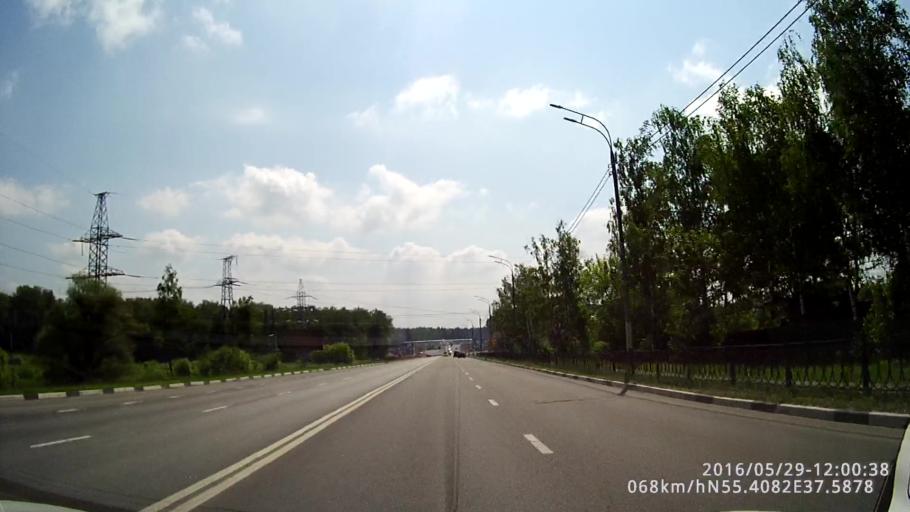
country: RU
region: Moskovskaya
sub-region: Podol'skiy Rayon
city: Podol'sk
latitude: 55.4079
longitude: 37.5883
